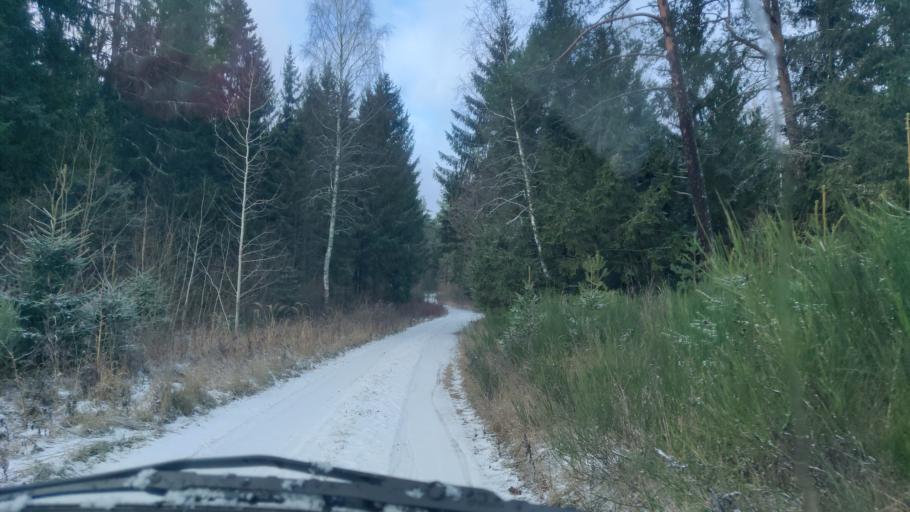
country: LT
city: Trakai
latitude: 54.5816
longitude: 24.9629
